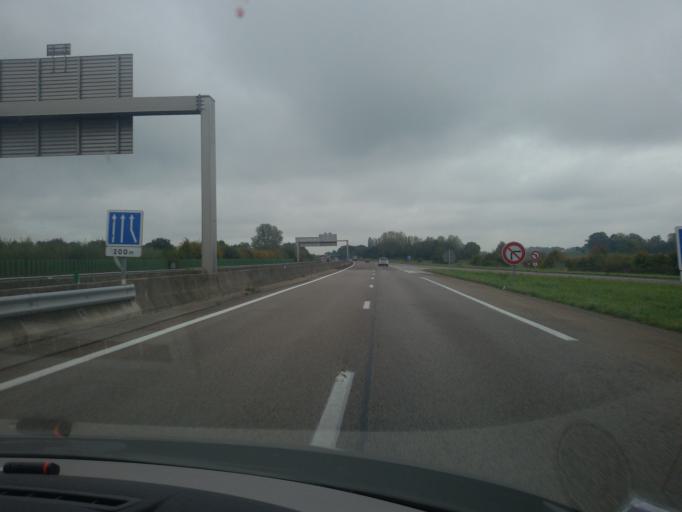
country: FR
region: Haute-Normandie
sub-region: Departement de l'Eure
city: Corneville-sur-Risle
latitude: 49.3800
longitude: 0.6129
